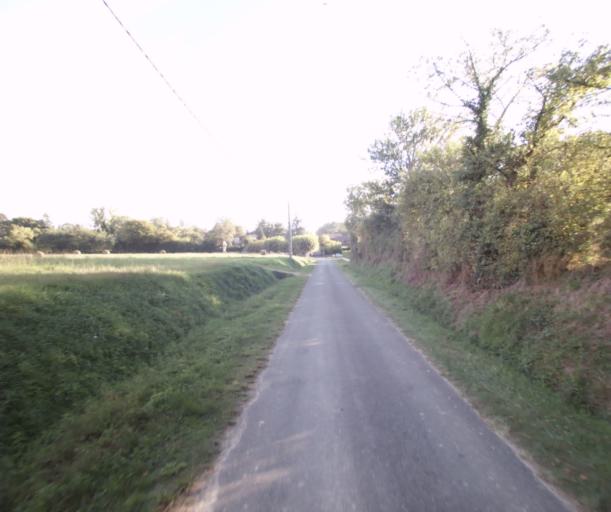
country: FR
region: Midi-Pyrenees
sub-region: Departement du Gers
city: Cazaubon
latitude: 43.8662
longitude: -0.0003
